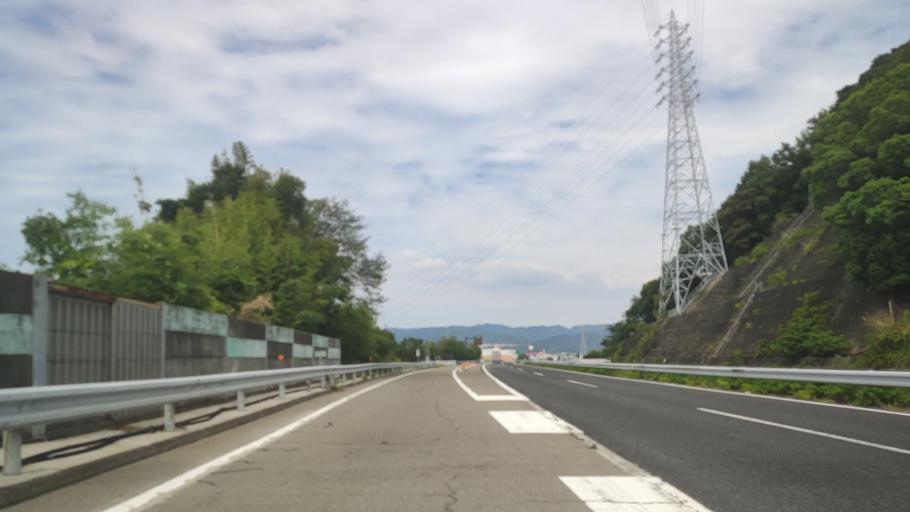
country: JP
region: Wakayama
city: Wakayama-shi
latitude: 34.2307
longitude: 135.2128
